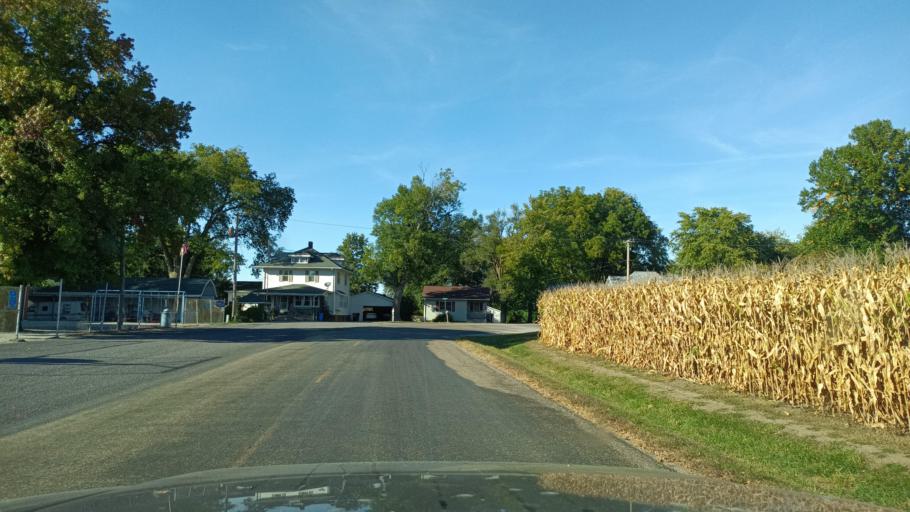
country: US
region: Illinois
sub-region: De Witt County
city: Clinton
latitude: 40.2237
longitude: -88.9595
